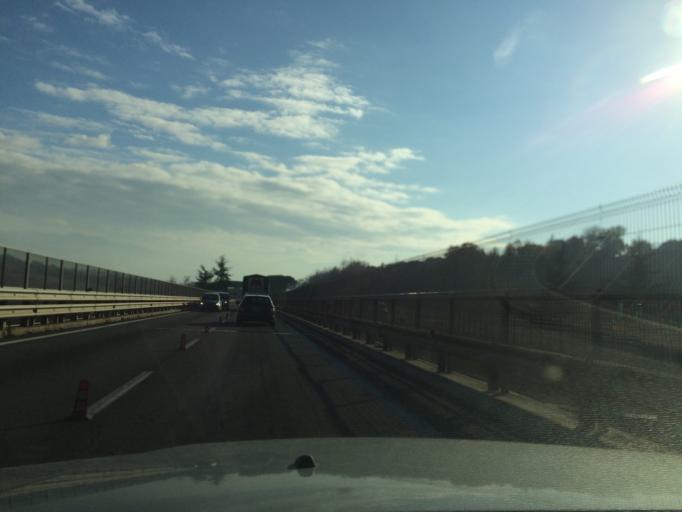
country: IT
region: Umbria
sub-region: Provincia di Terni
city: San Gemini
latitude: 42.6233
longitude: 12.5515
